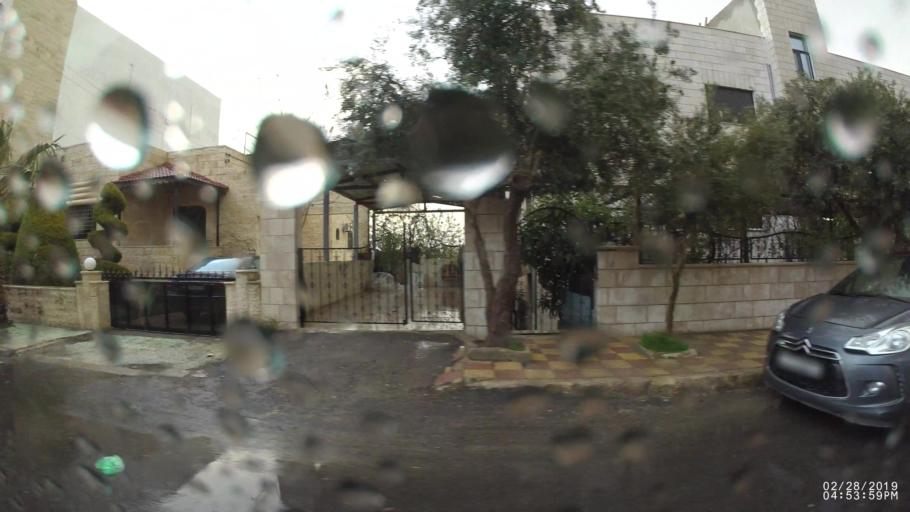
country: JO
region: Amman
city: Amman
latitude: 32.0028
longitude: 35.9288
